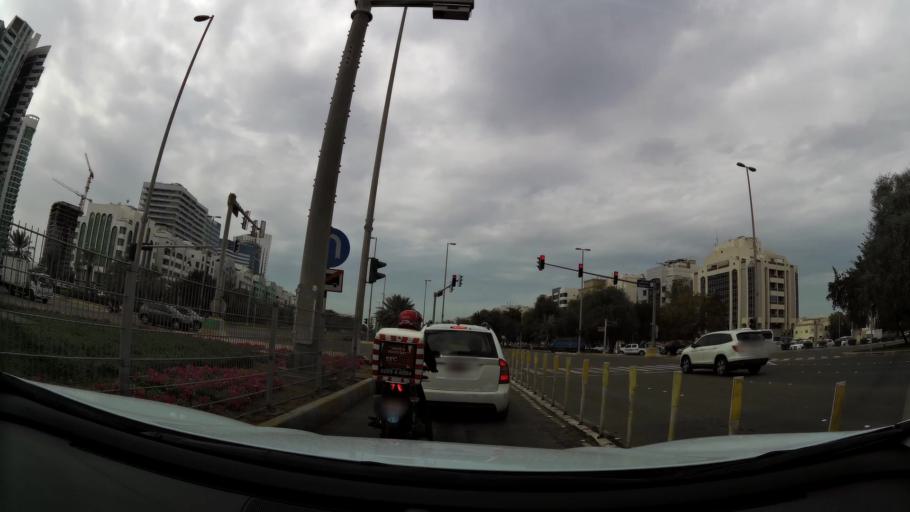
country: AE
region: Abu Dhabi
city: Abu Dhabi
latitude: 24.4328
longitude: 54.4388
